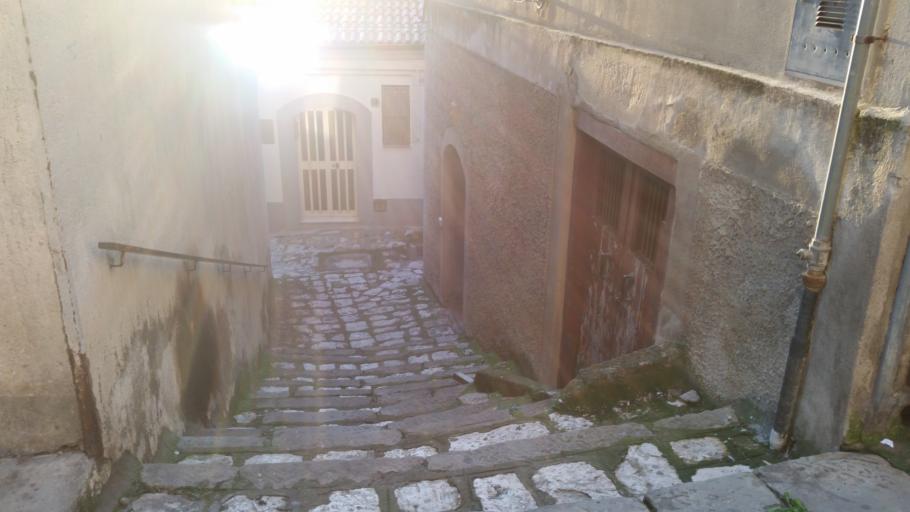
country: IT
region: Basilicate
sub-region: Provincia di Matera
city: Tricarico
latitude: 40.6205
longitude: 16.1465
